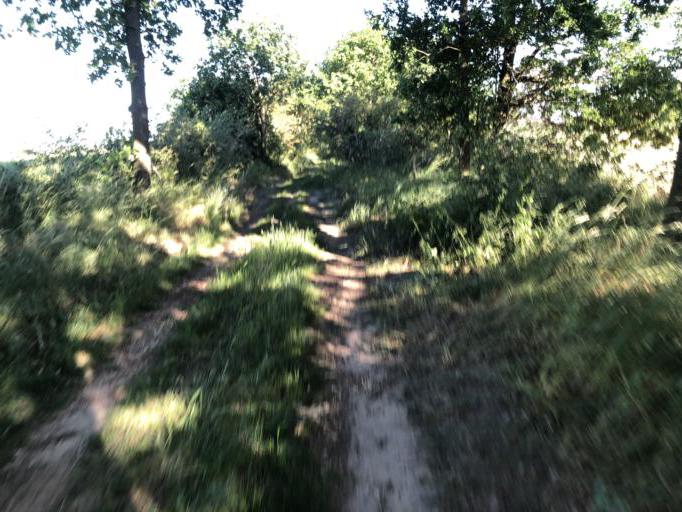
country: DE
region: Brandenburg
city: Schonefeld
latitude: 52.3464
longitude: 13.4986
